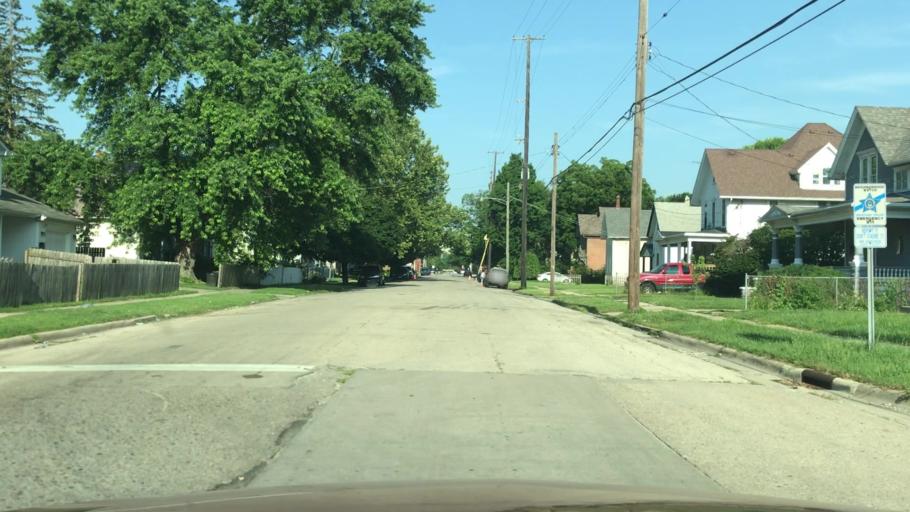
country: US
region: Illinois
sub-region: Winnebago County
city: Rockford
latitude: 42.2627
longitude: -89.0771
